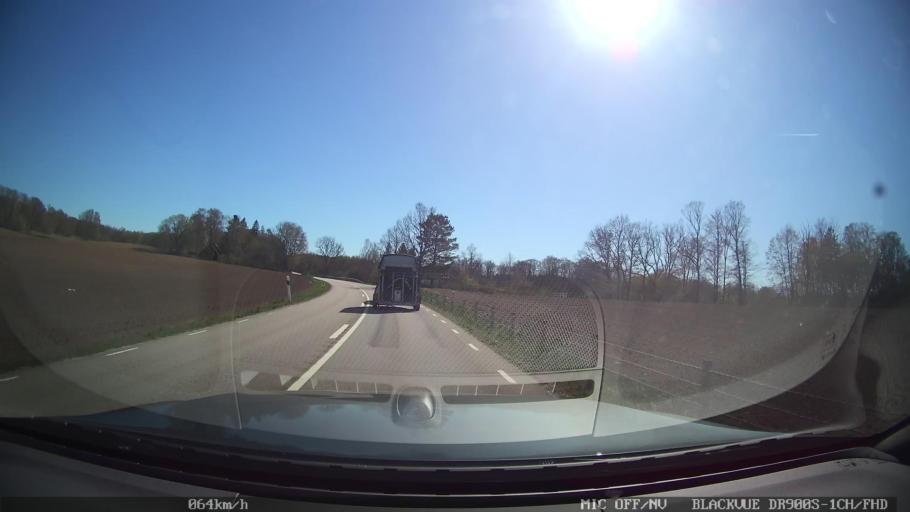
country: SE
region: Skane
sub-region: Klippans Kommun
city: Ljungbyhed
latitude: 56.1042
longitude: 13.1767
